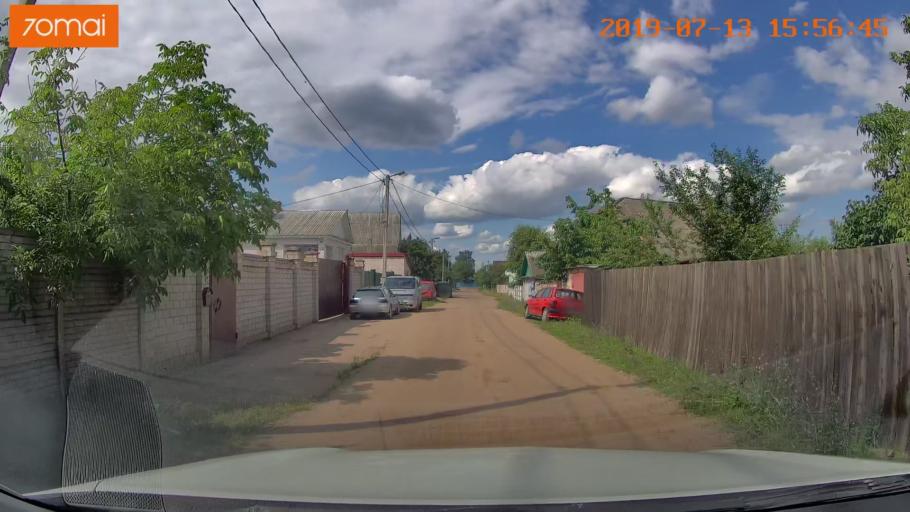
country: BY
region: Mogilev
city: Babruysk
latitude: 53.1447
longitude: 29.2023
